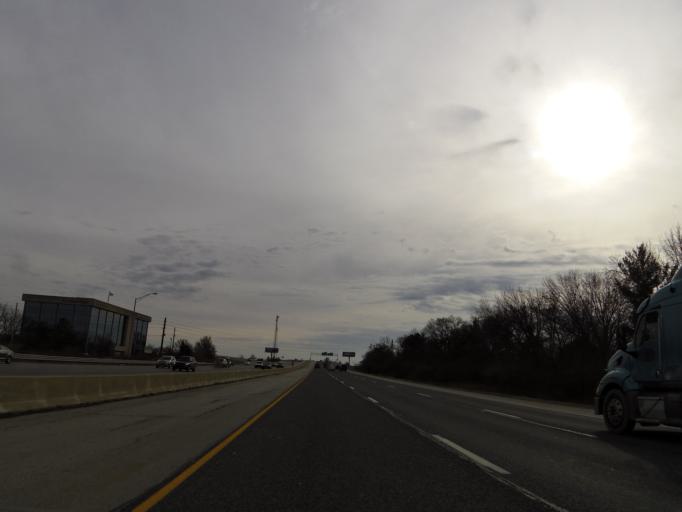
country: US
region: Indiana
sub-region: Marion County
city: Lawrence
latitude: 39.9000
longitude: -86.0622
